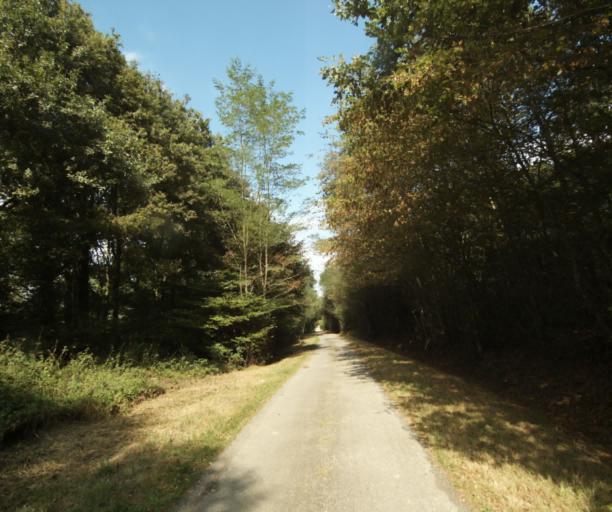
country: FR
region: Bourgogne
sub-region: Departement de Saone-et-Loire
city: Palinges
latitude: 46.5063
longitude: 4.2243
